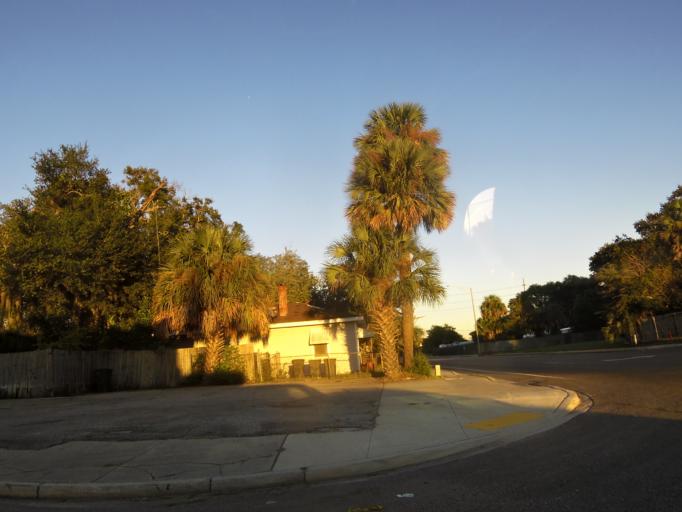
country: US
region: Florida
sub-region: Duval County
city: Jacksonville
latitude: 30.3453
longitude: -81.6410
